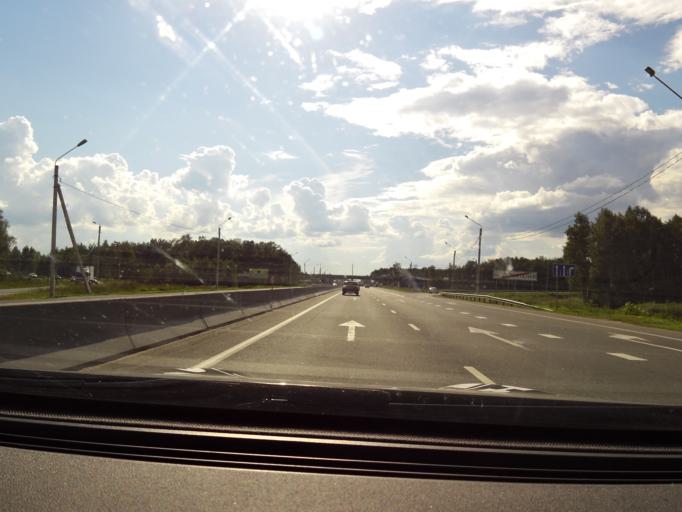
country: RU
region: Nizjnij Novgorod
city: Gorbatovka
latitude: 56.3069
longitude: 43.6911
